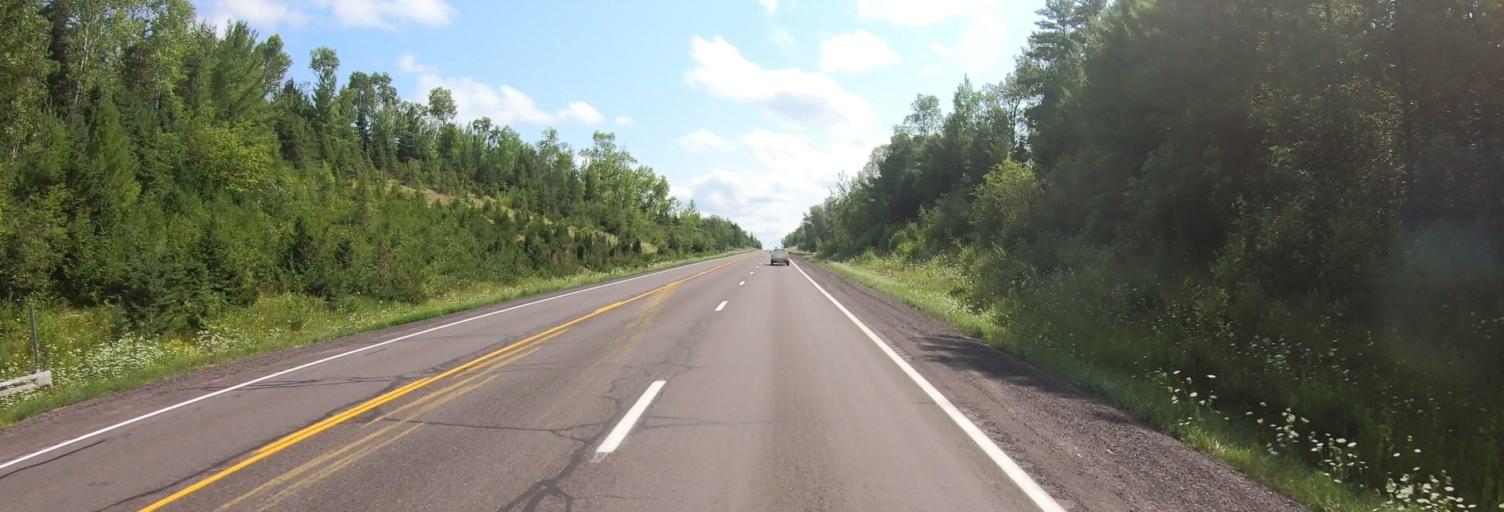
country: US
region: Michigan
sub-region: Ontonagon County
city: Ontonagon
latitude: 46.6795
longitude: -89.1663
